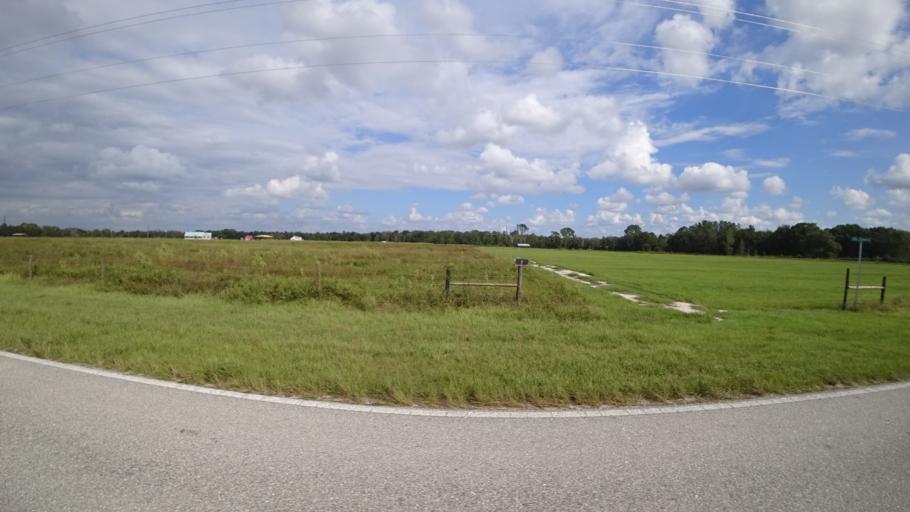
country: US
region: Florida
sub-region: Hillsborough County
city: Wimauma
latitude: 27.5911
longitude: -82.1987
